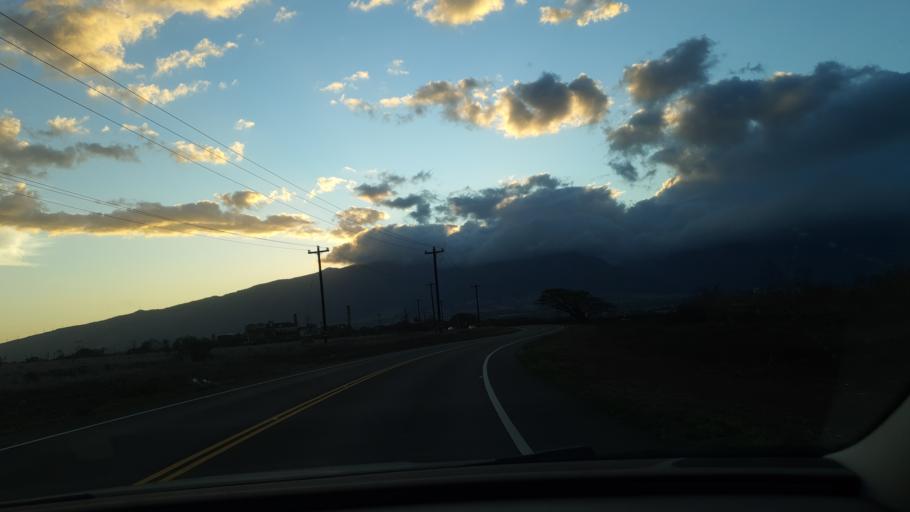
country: US
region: Hawaii
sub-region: Maui County
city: Kahului
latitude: 20.8711
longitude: -156.4442
